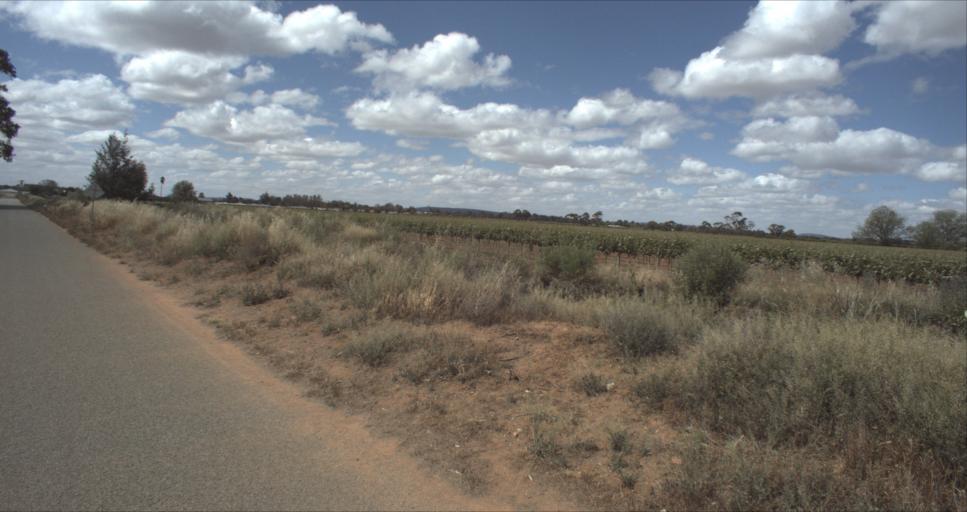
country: AU
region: New South Wales
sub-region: Leeton
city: Leeton
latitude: -34.5767
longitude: 146.3981
